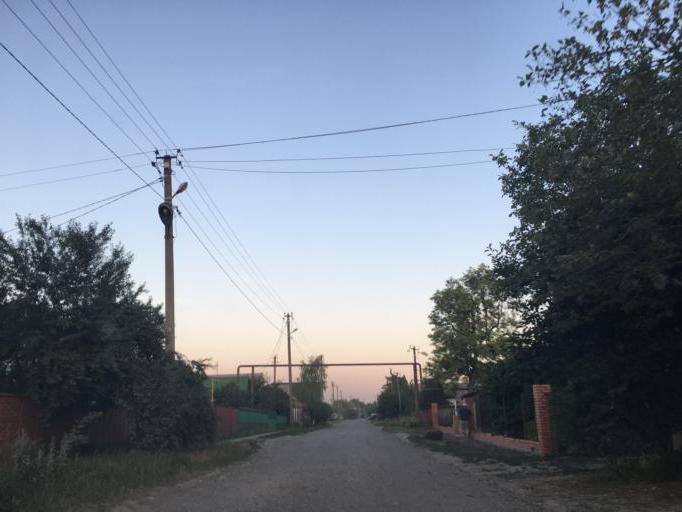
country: RU
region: Krasnodarskiy
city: Kushchevskaya
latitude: 46.5653
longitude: 39.6393
